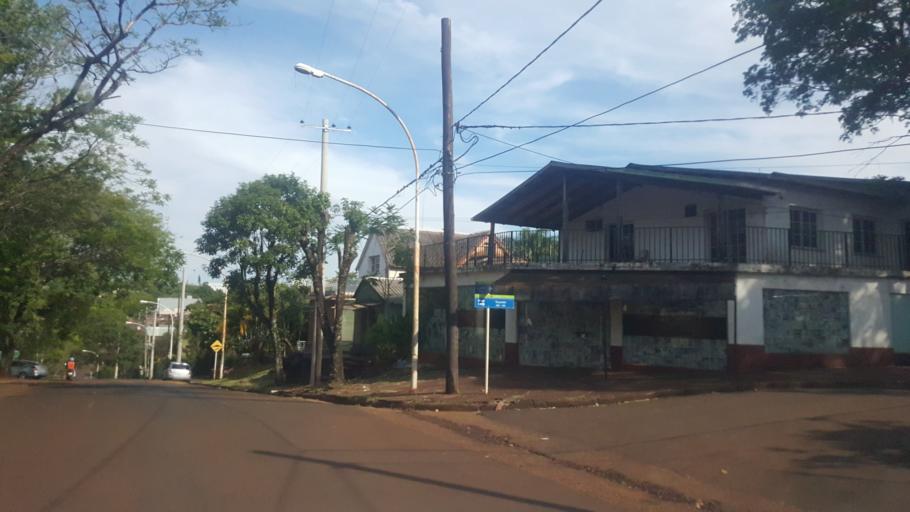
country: AR
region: Misiones
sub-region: Departamento de Leandro N. Alem
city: Leandro N. Alem
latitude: -27.6009
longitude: -55.3292
